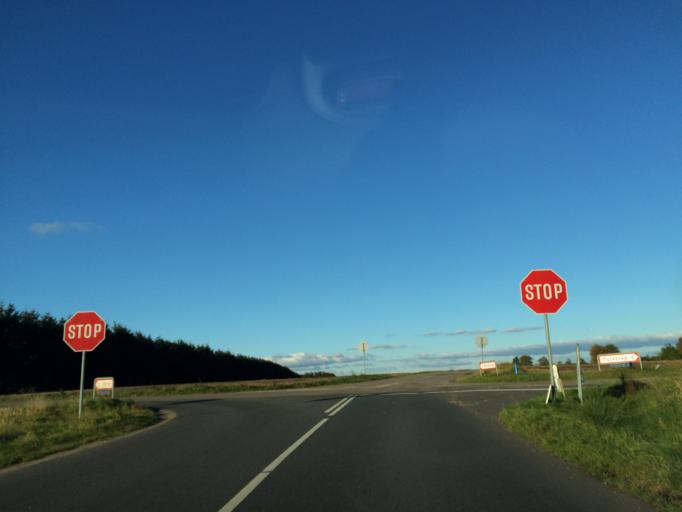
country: DK
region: Central Jutland
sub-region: Skanderborg Kommune
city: Ry
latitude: 56.1347
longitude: 9.7198
